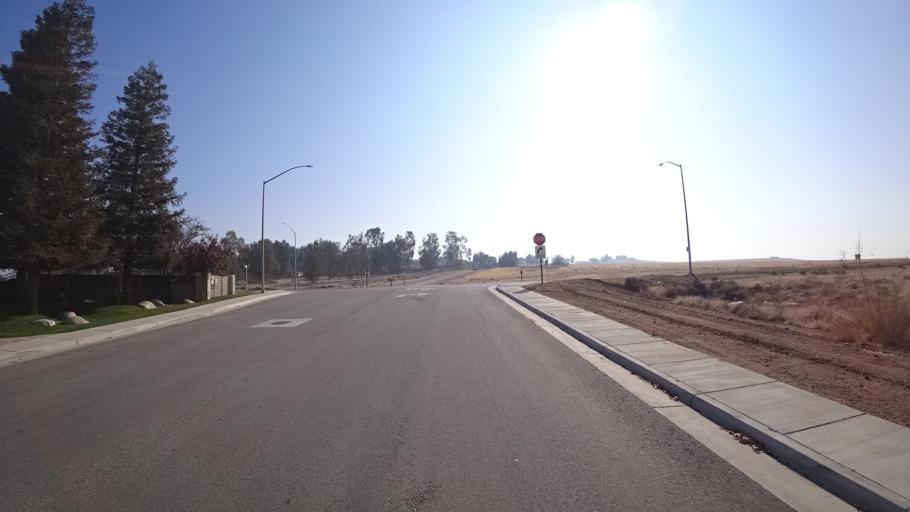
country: US
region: California
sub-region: Kern County
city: Oildale
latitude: 35.4046
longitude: -118.8703
